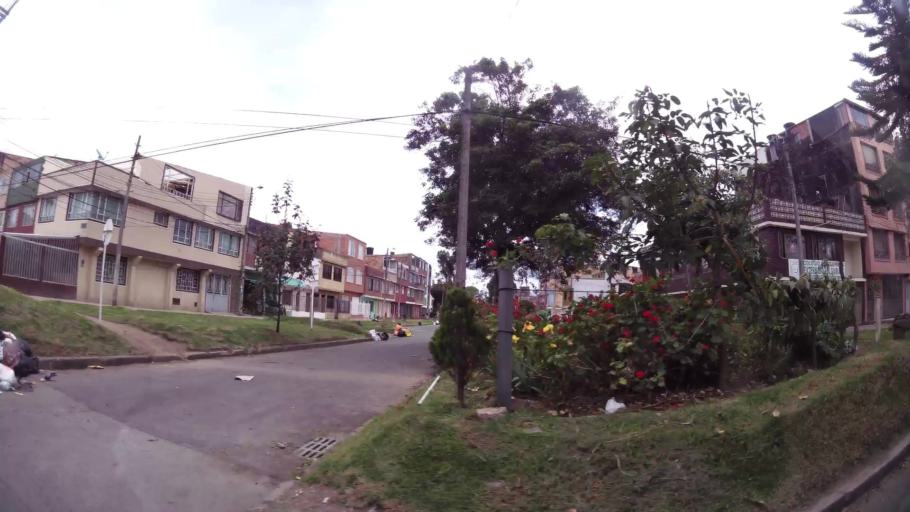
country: CO
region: Cundinamarca
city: Funza
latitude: 4.7095
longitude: -74.1219
